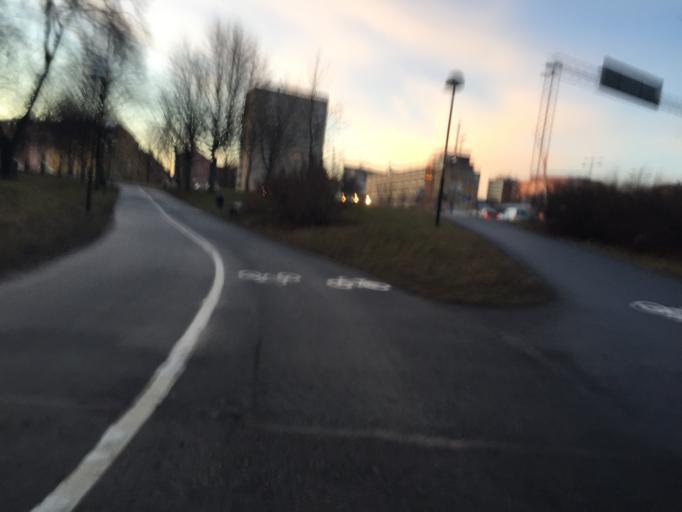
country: SE
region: Stockholm
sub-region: Solna Kommun
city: Solna
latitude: 59.3306
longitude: 18.0206
